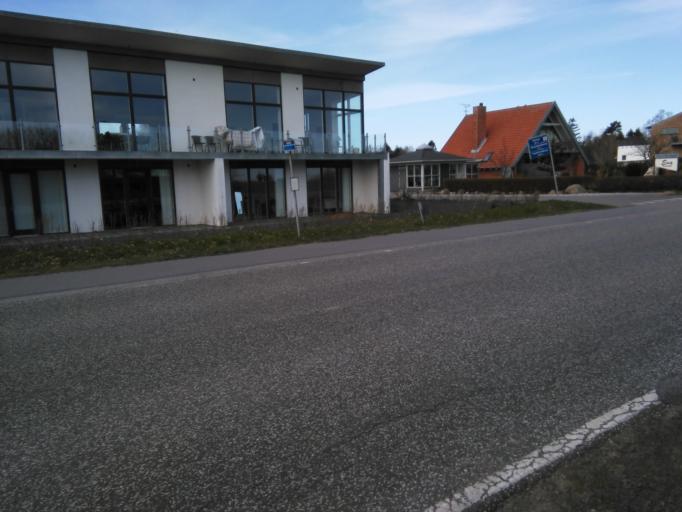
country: DK
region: Central Jutland
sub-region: Arhus Kommune
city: Malling
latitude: 55.9888
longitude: 10.2510
